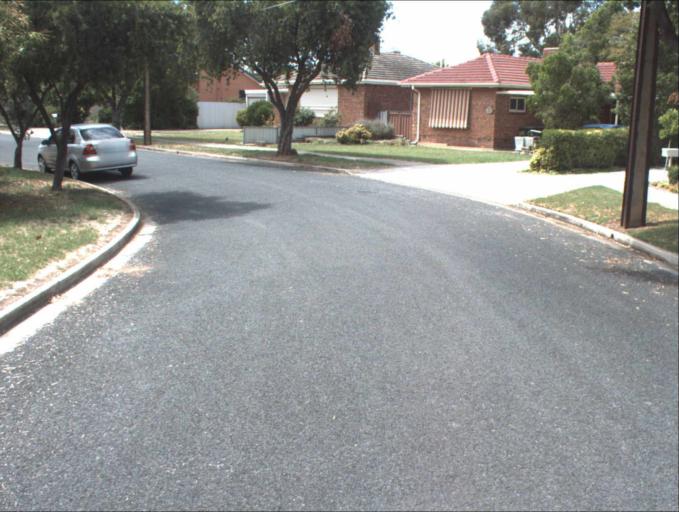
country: AU
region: South Australia
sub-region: Port Adelaide Enfield
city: Enfield
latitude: -34.8548
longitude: 138.6165
